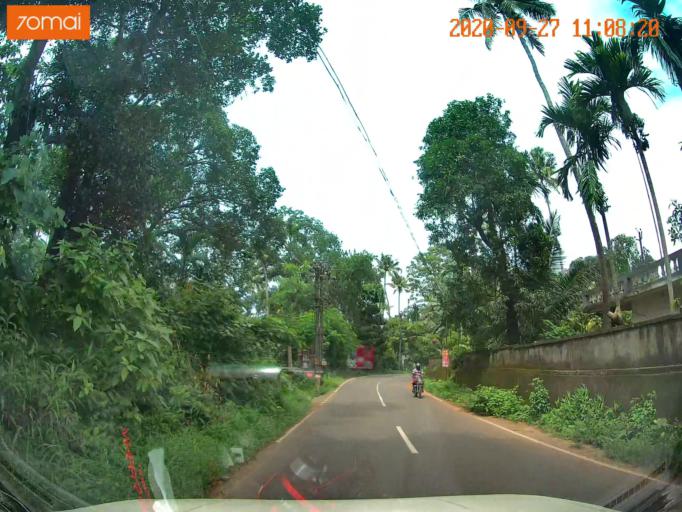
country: IN
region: Kerala
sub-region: Thrissur District
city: Trichur
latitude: 10.4302
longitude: 76.2335
